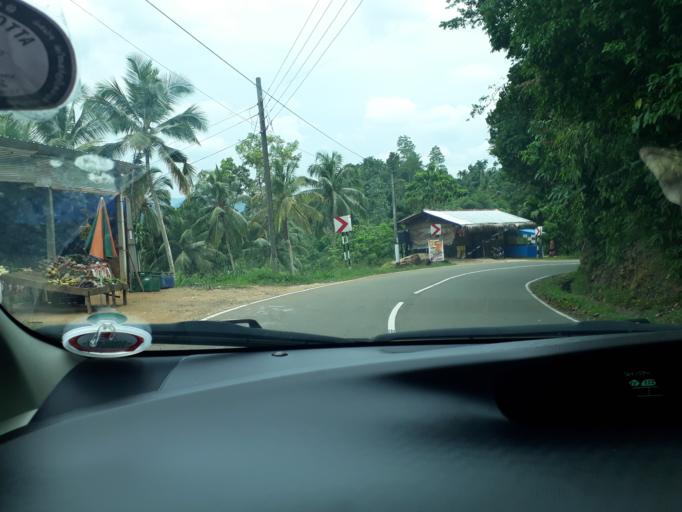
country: LK
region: Southern
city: Weligama
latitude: 6.3114
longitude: 80.5439
